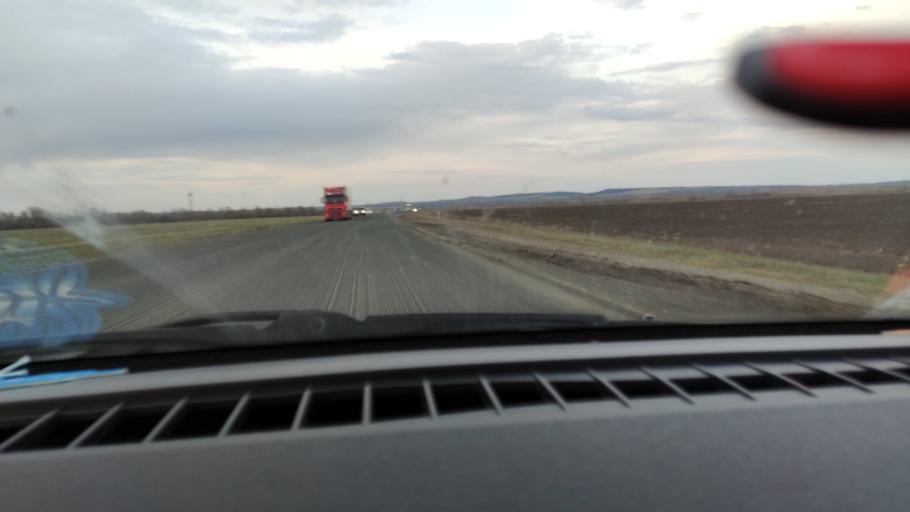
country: RU
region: Saratov
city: Yelshanka
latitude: 51.8132
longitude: 46.2058
